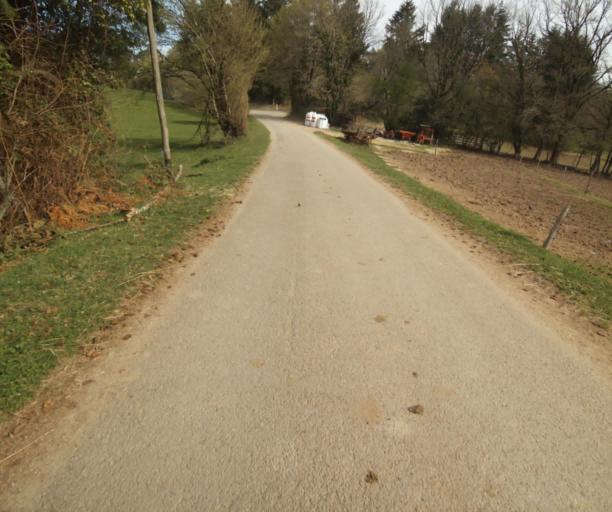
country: FR
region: Limousin
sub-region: Departement de la Correze
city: Correze
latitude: 45.3817
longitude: 1.8223
